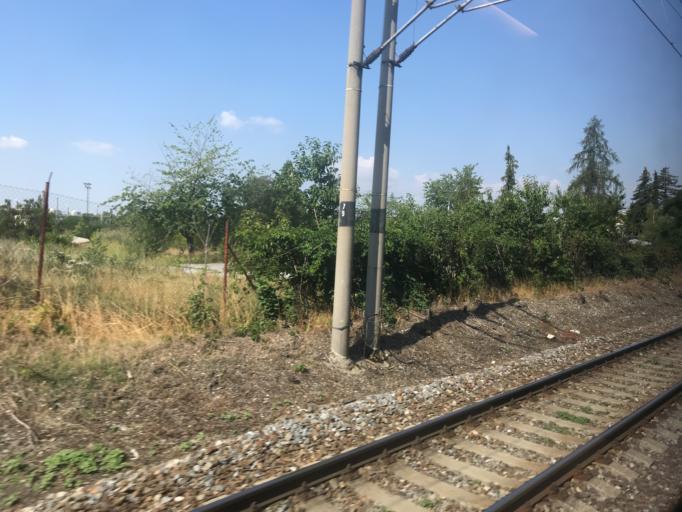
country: CZ
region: Praha
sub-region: Praha 9
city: Vysocany
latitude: 50.0641
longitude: 14.4996
